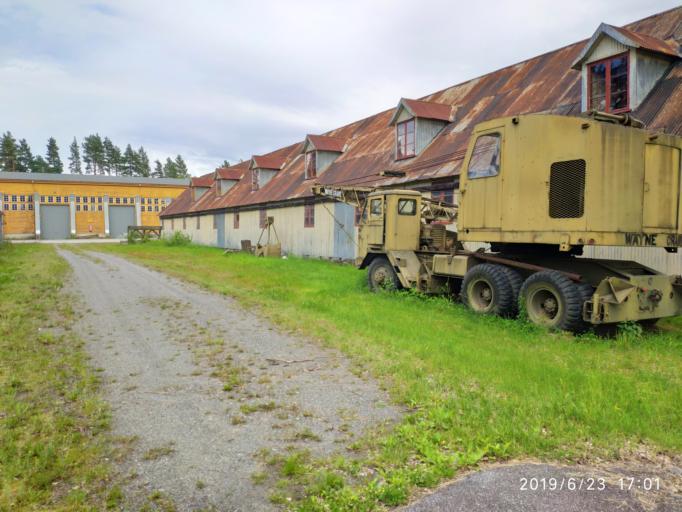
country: NO
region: Buskerud
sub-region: Ringerike
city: Honefoss
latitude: 60.1923
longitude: 10.2909
